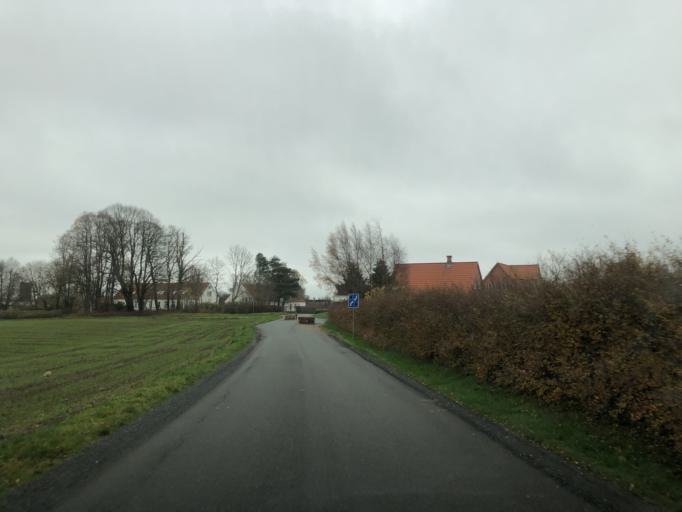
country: DK
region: Central Jutland
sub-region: Skanderborg Kommune
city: Ry
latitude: 56.0722
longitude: 9.8370
